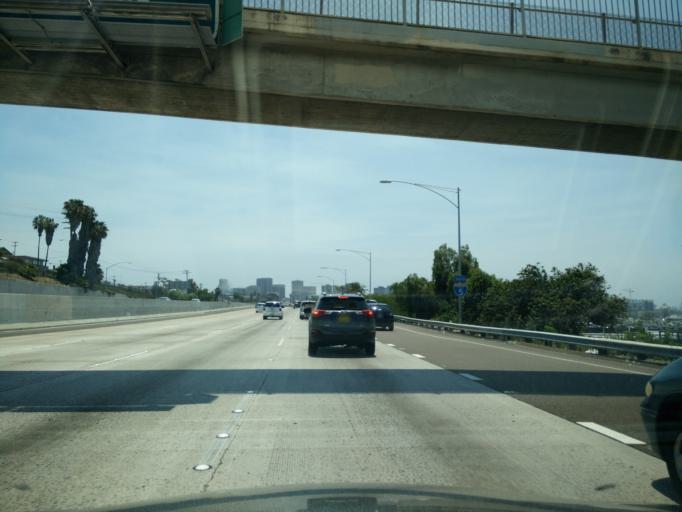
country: US
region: California
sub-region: San Diego County
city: San Diego
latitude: 32.7337
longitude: -117.1736
